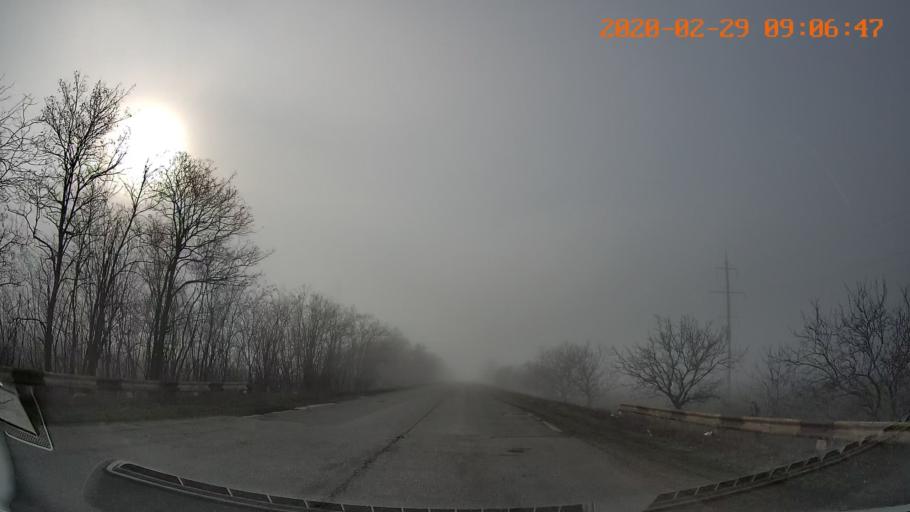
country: MD
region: Telenesti
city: Tiraspolul Nou
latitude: 46.8710
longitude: 29.7461
